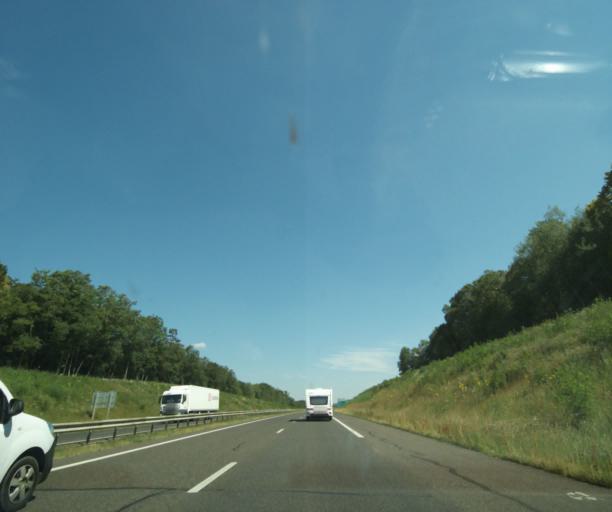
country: FR
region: Lorraine
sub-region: Departement de Meurthe-et-Moselle
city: Dommartin-les-Toul
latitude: 48.6382
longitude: 5.8808
